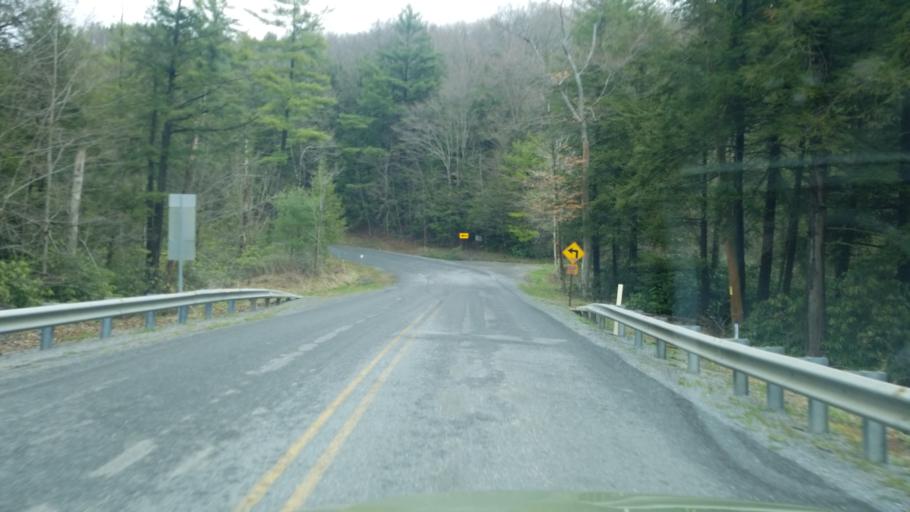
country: US
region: Pennsylvania
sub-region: Clearfield County
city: Clearfield
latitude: 41.0639
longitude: -78.4182
